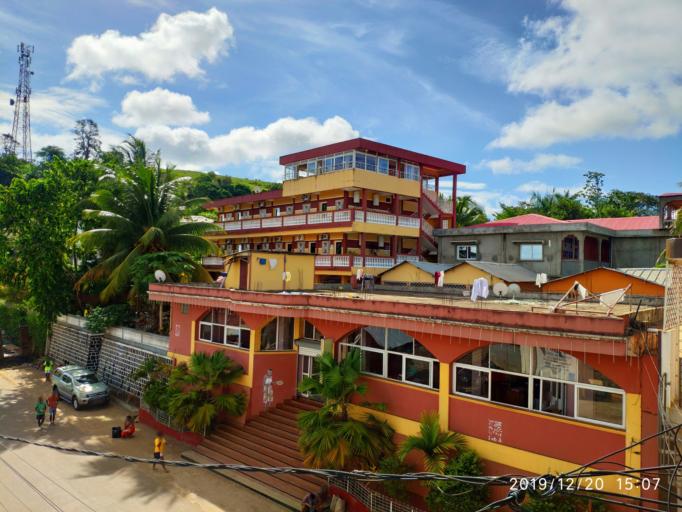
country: MG
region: Diana
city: Hell-Ville
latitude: -13.3930
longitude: 48.2708
